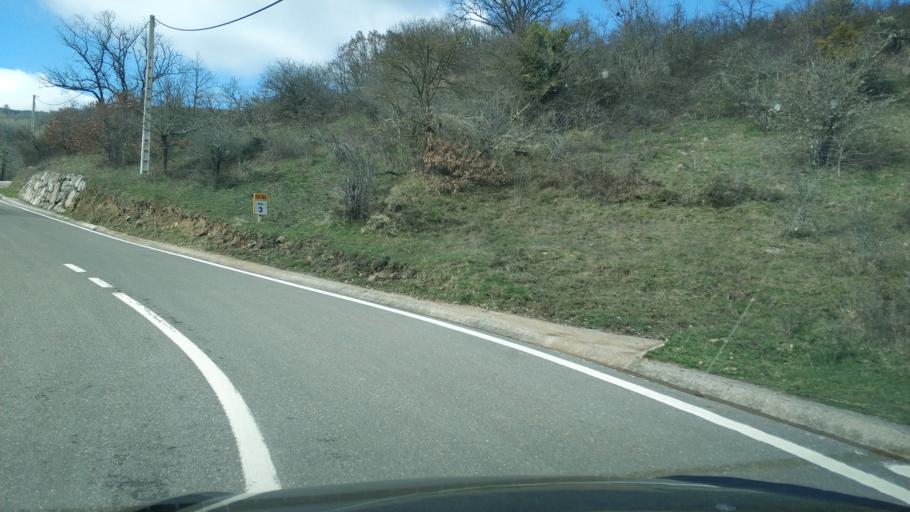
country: ES
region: Castille and Leon
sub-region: Provincia de Palencia
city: Berzosilla
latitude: 42.9017
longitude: -4.0346
